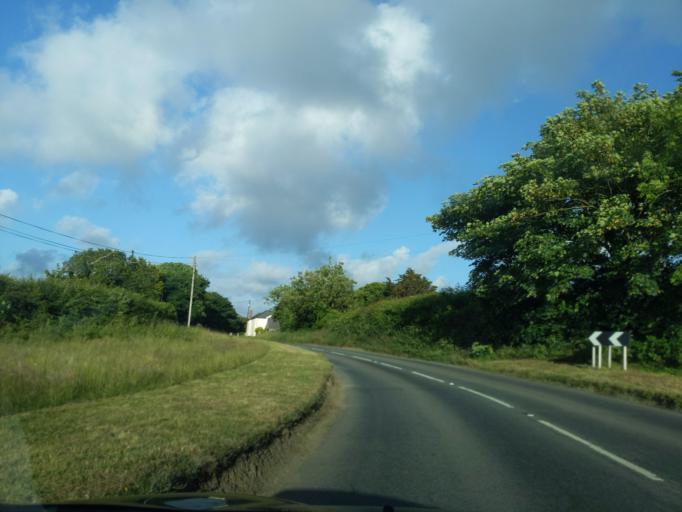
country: GB
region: England
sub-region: Devon
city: Fremington
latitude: 51.0064
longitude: -4.1124
